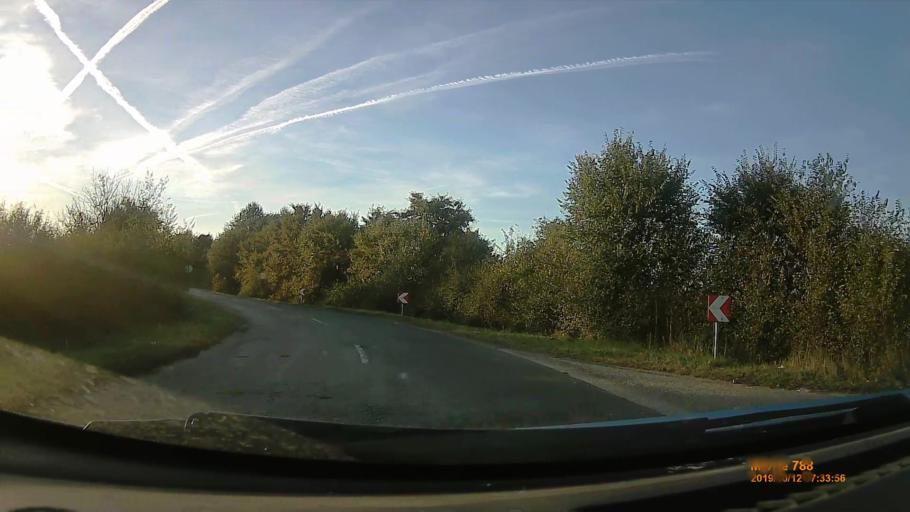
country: HU
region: Hajdu-Bihar
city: Pocsaj
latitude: 47.2658
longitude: 21.7998
